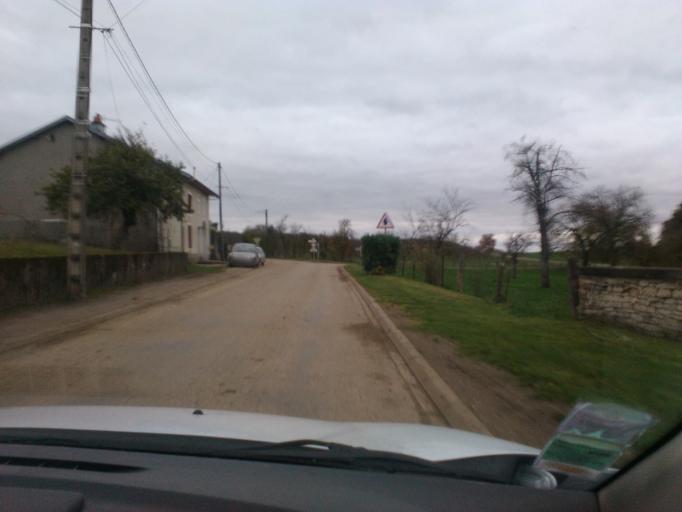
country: FR
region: Lorraine
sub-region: Departement des Vosges
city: Mirecourt
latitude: 48.2830
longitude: 6.1958
